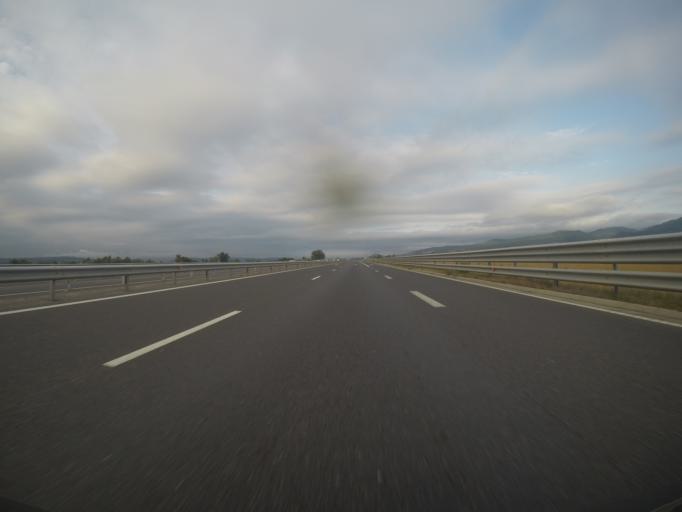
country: RO
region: Hunedoara
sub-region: Comuna Turdas
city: Pricaz
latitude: 45.8786
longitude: 23.1957
